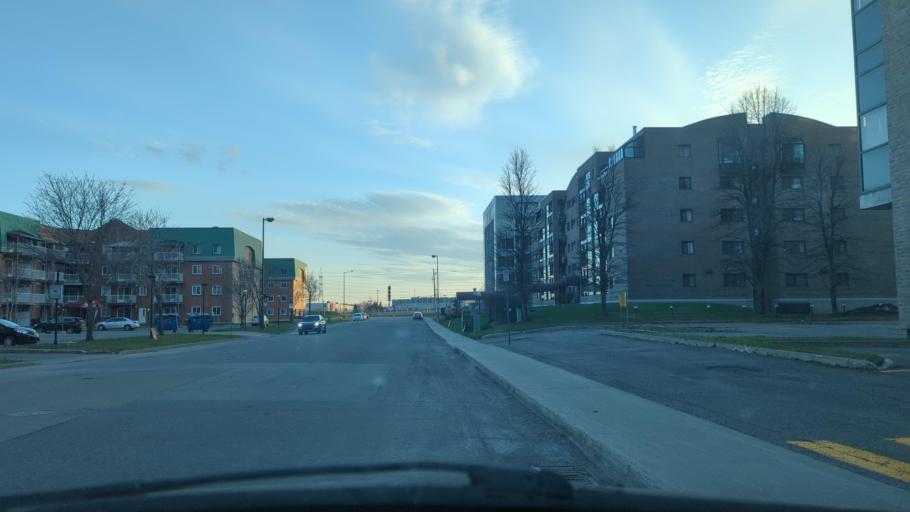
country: CA
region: Quebec
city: Quebec
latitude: 46.8458
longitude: -71.2683
